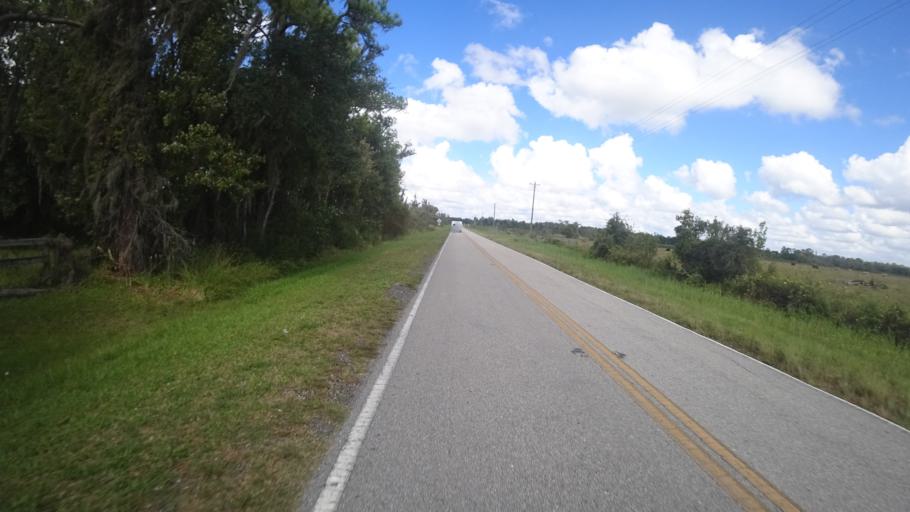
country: US
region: Florida
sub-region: Sarasota County
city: Lake Sarasota
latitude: 27.4030
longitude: -82.1315
